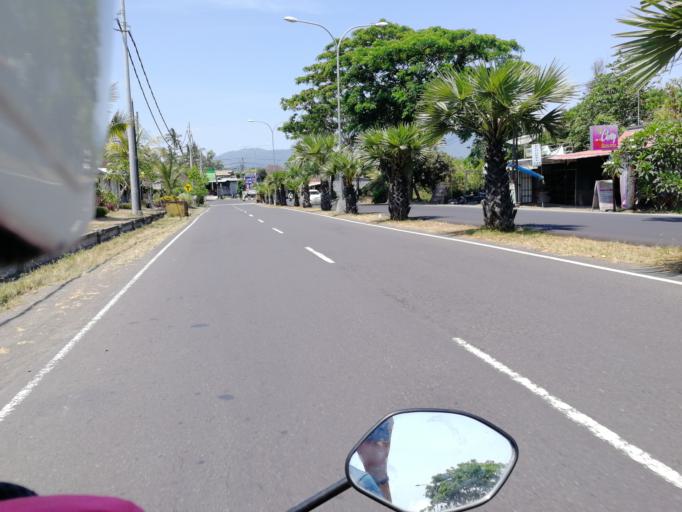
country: ID
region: Bali
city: Subagan
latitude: -8.4389
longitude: 115.5932
